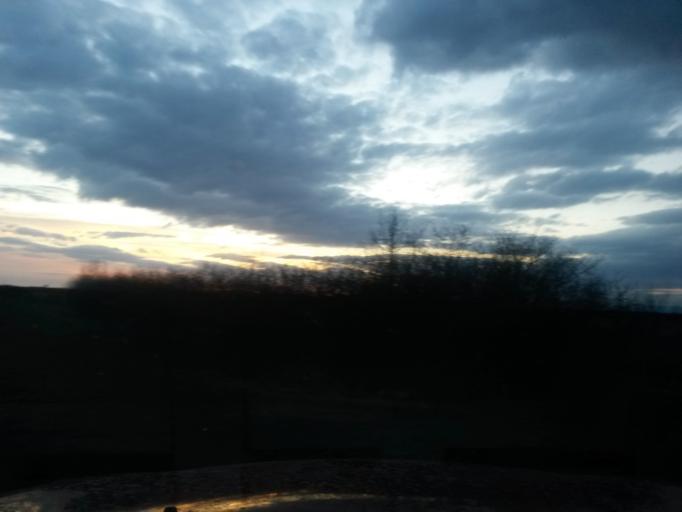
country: SK
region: Kosicky
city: Sobrance
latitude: 48.6970
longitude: 22.0550
